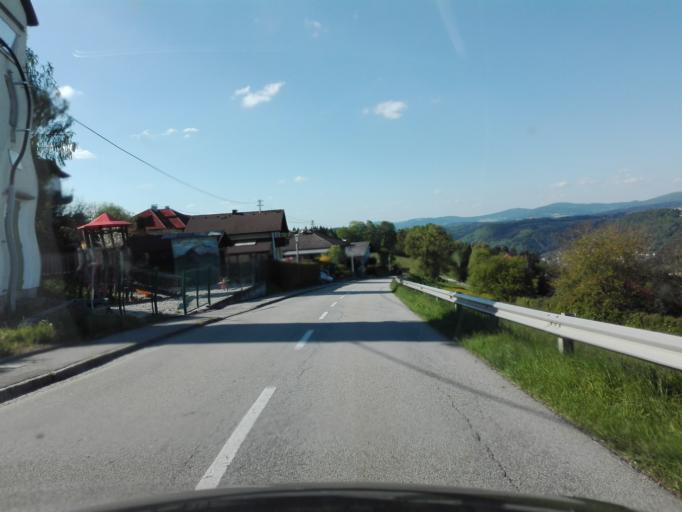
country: DE
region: Bavaria
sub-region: Lower Bavaria
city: Obernzell
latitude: 48.5317
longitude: 13.6471
